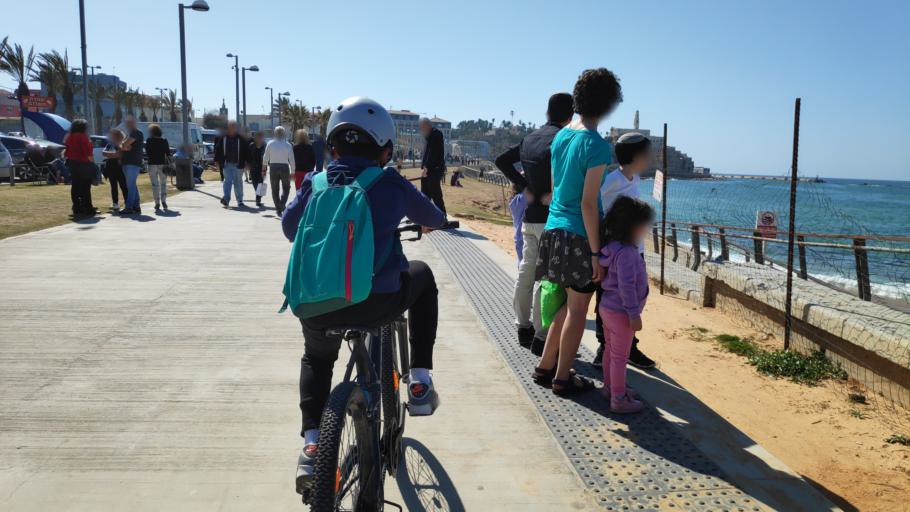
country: IL
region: Tel Aviv
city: Yafo
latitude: 32.0580
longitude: 34.7577
